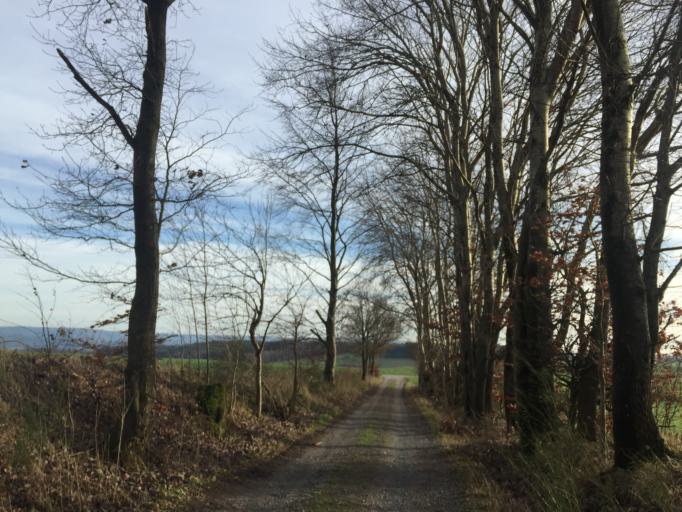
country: DE
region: Hesse
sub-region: Regierungsbezirk Darmstadt
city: Erbach
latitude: 49.6861
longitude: 8.9357
